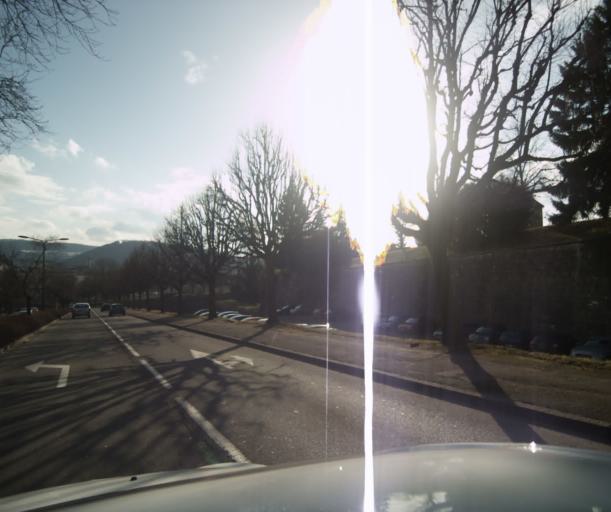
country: FR
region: Franche-Comte
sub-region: Departement du Doubs
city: Besancon
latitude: 47.2445
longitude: 6.0237
